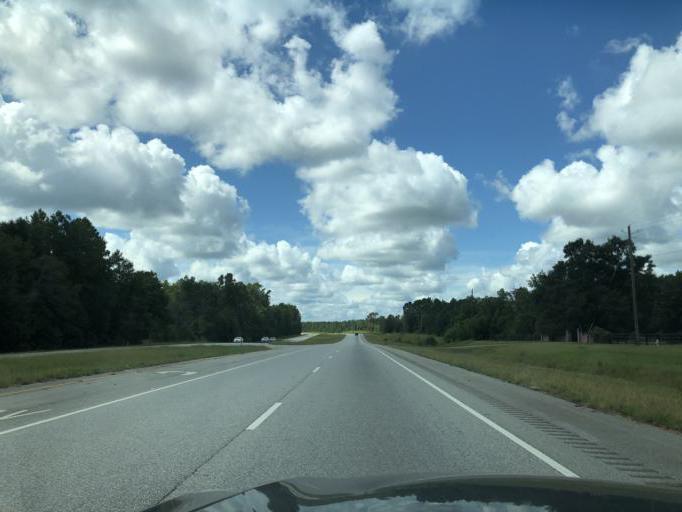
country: US
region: Alabama
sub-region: Russell County
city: Ladonia
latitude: 32.2408
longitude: -85.1678
